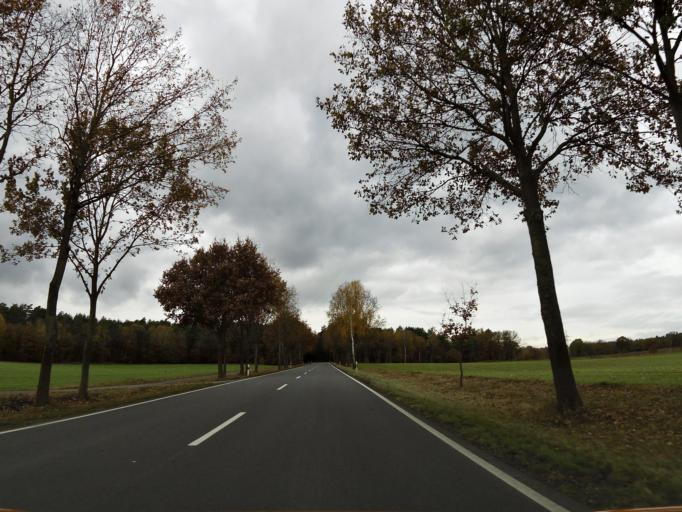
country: DE
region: Lower Saxony
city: Schnega
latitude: 52.9164
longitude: 10.8871
